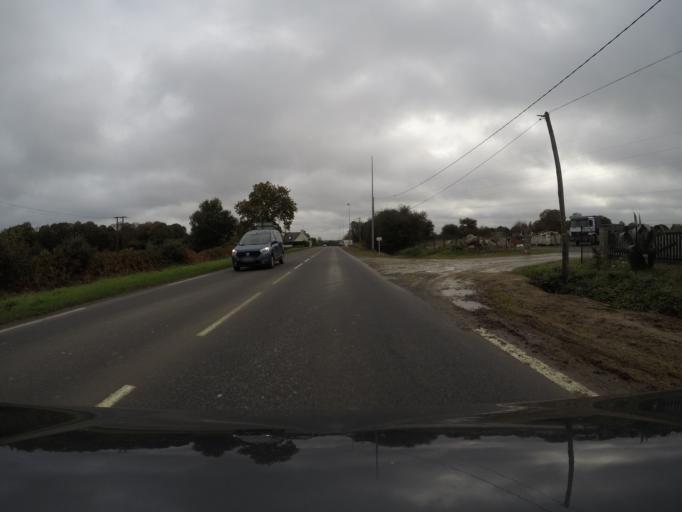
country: FR
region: Brittany
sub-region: Departement des Cotes-d'Armor
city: Graces
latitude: 48.5663
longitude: -3.1880
